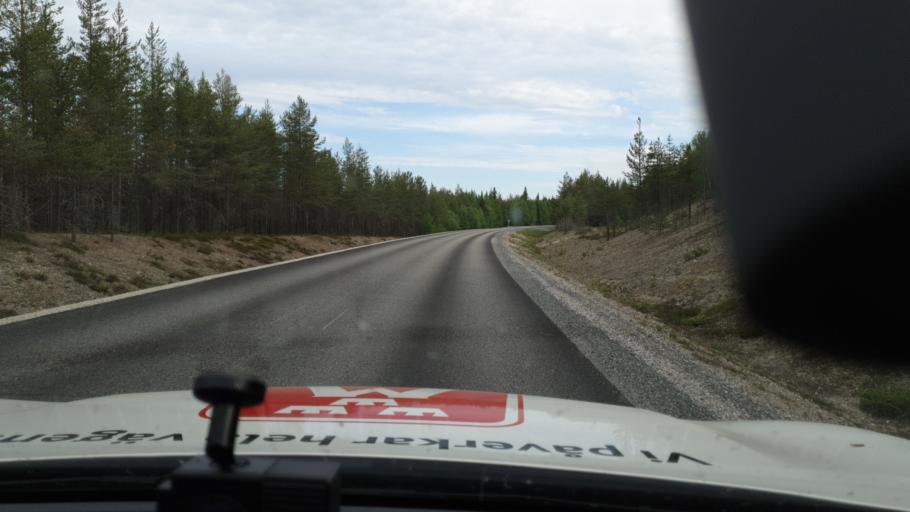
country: SE
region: Vaesterbotten
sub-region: Mala Kommun
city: Mala
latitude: 64.9257
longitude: 18.6182
